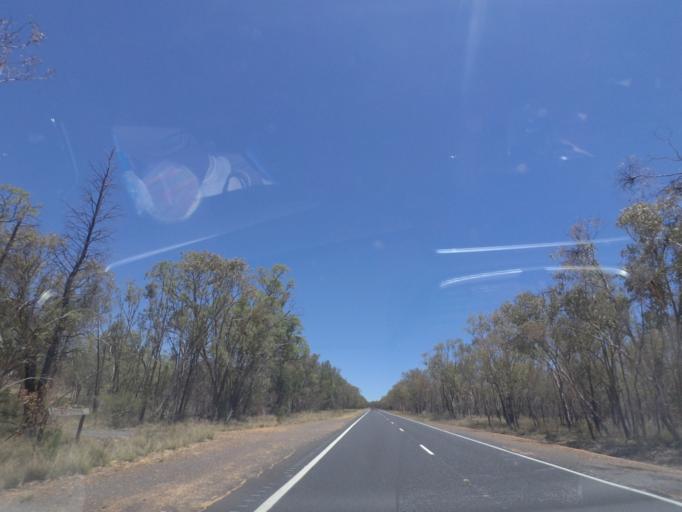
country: AU
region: New South Wales
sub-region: Warrumbungle Shire
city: Coonabarabran
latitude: -31.1720
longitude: 149.3604
